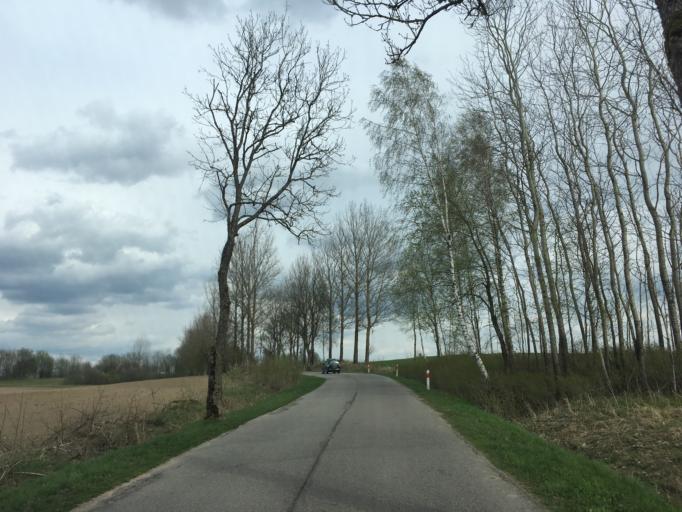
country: PL
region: Podlasie
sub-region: Powiat suwalski
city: Filipow
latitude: 54.3546
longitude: 22.7520
